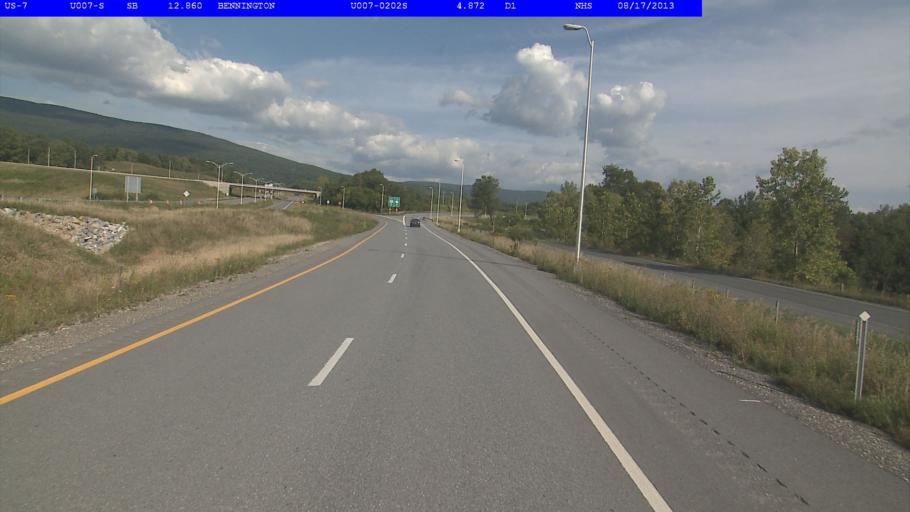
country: US
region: Vermont
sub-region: Bennington County
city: Bennington
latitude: 42.9025
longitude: -73.2045
